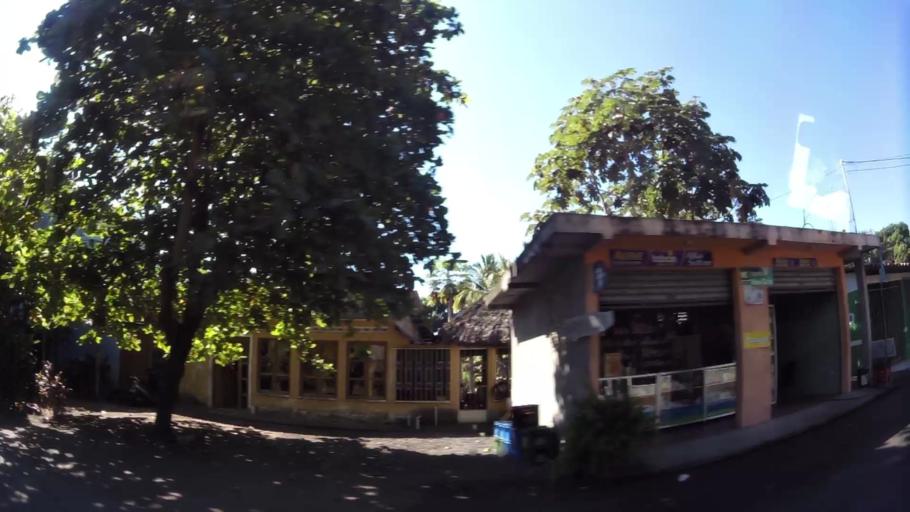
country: GT
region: Santa Rosa
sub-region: Municipio de Taxisco
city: Taxisco
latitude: 13.9075
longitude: -90.5170
